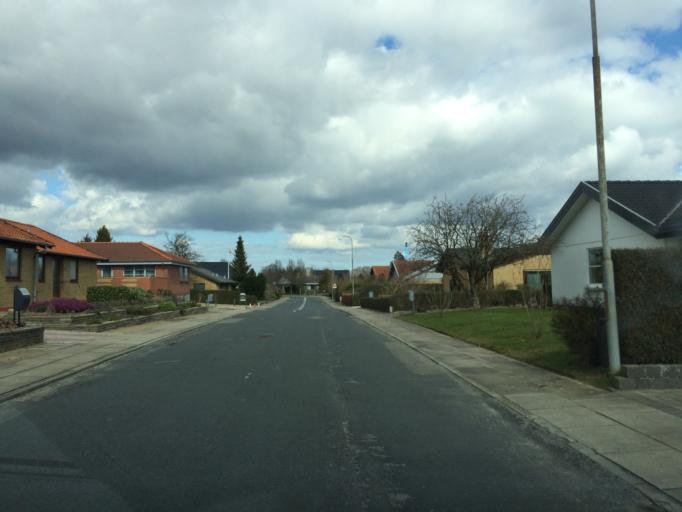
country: DK
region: South Denmark
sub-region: Nordfyns Kommune
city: Sonderso
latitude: 55.4164
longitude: 10.2751
